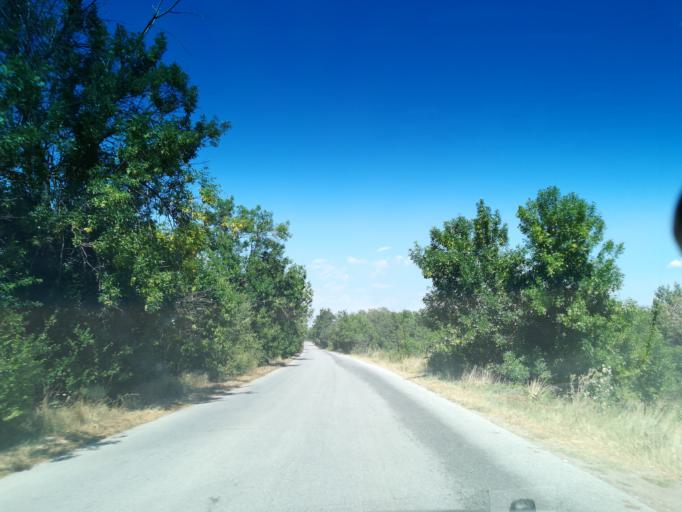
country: BG
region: Stara Zagora
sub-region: Obshtina Chirpan
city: Chirpan
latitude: 42.0671
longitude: 25.1756
